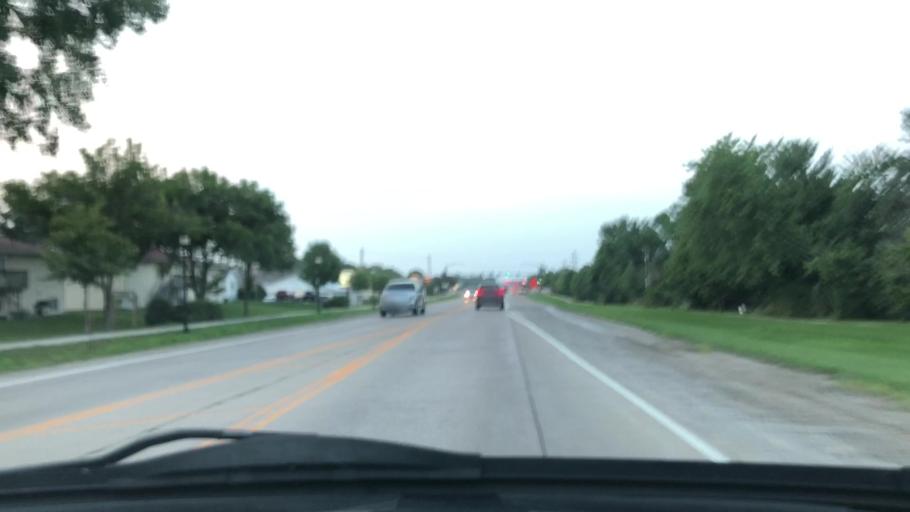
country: US
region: Iowa
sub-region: Johnson County
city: North Liberty
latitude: 41.7421
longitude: -91.6076
